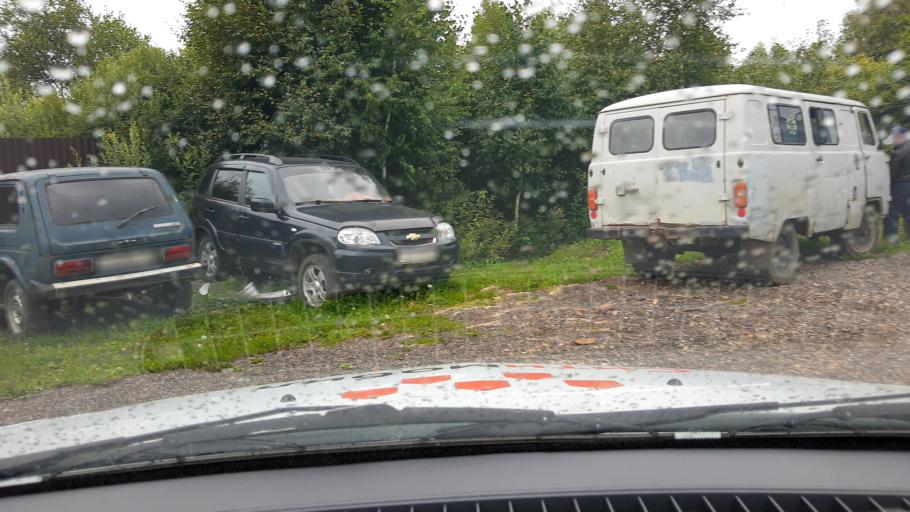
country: RU
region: Bashkortostan
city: Krasnaya Gorka
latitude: 55.1850
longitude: 56.6820
